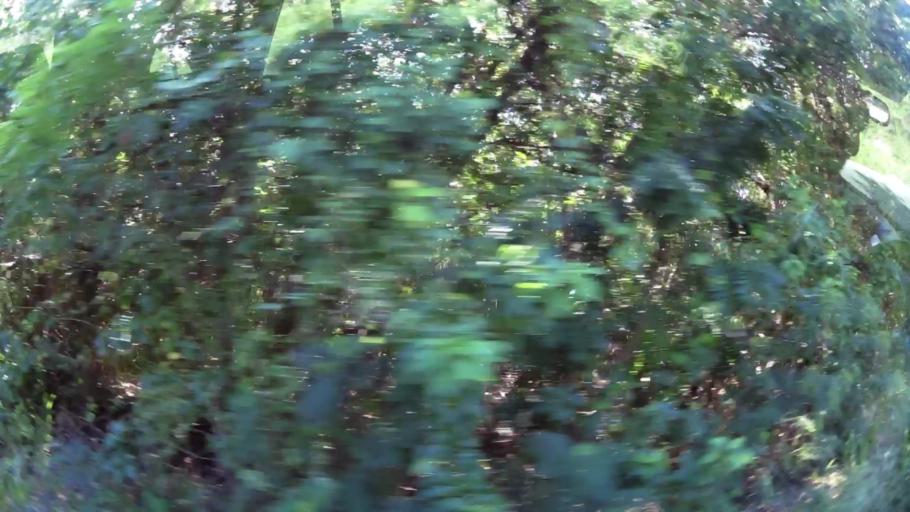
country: VG
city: Tortola
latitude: 18.4137
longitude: -64.5916
